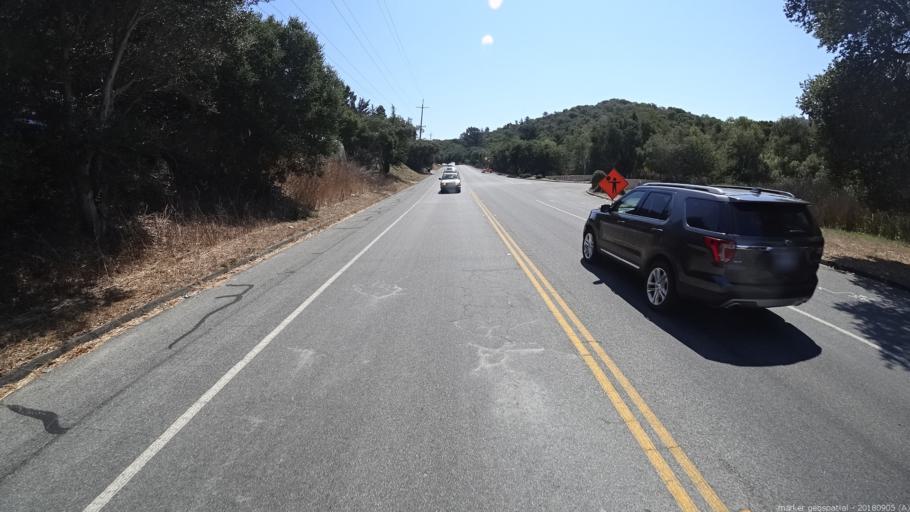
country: US
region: California
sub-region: Monterey County
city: Carmel Valley Village
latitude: 36.5655
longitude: -121.7537
